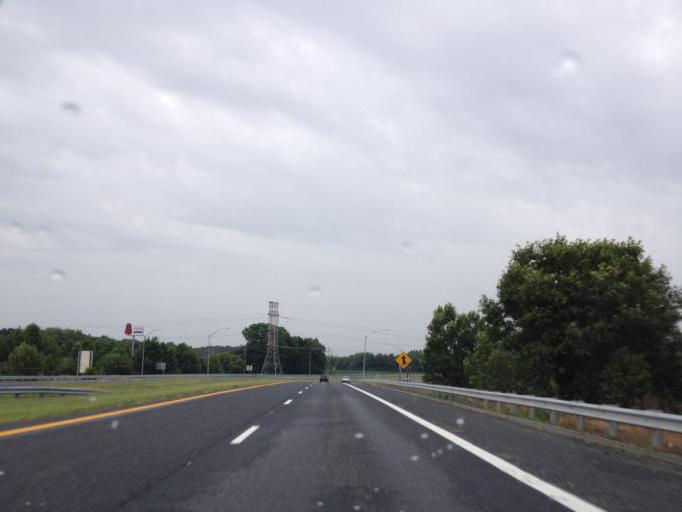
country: US
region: Maryland
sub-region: Caroline County
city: Denton
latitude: 38.8948
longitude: -75.8190
